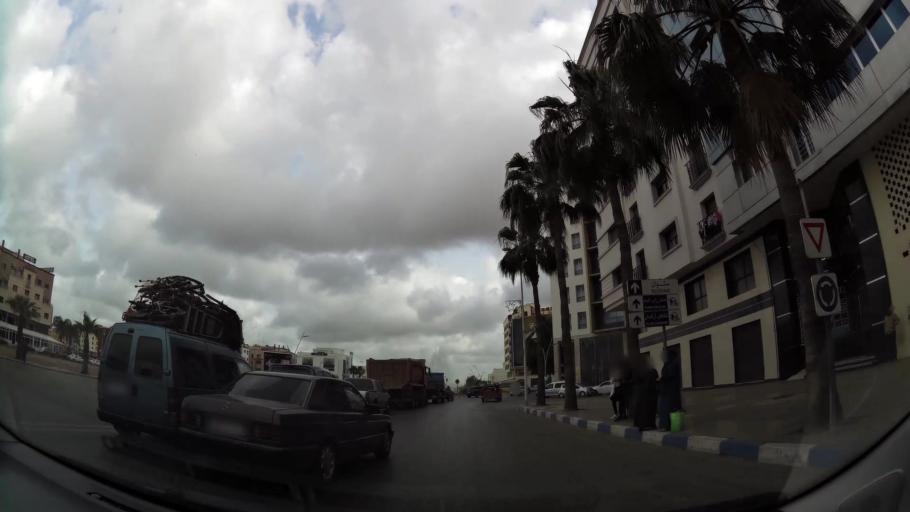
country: MA
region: Oriental
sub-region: Nador
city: Nador
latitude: 35.1528
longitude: -2.9289
